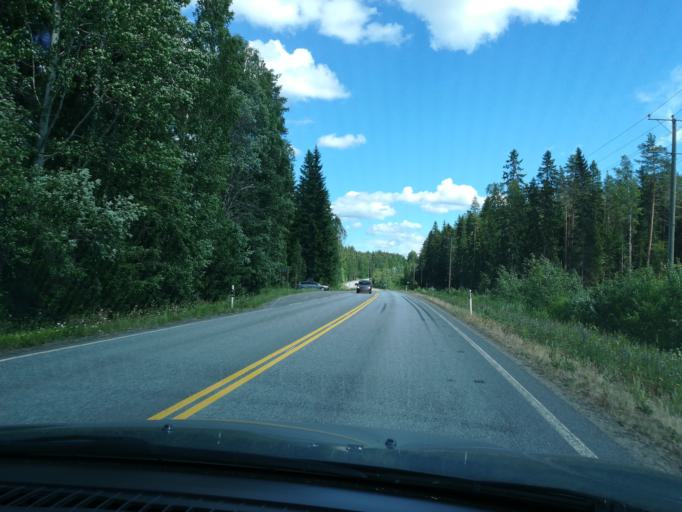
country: FI
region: Southern Savonia
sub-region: Mikkeli
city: Hirvensalmi
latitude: 61.6553
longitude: 27.0034
